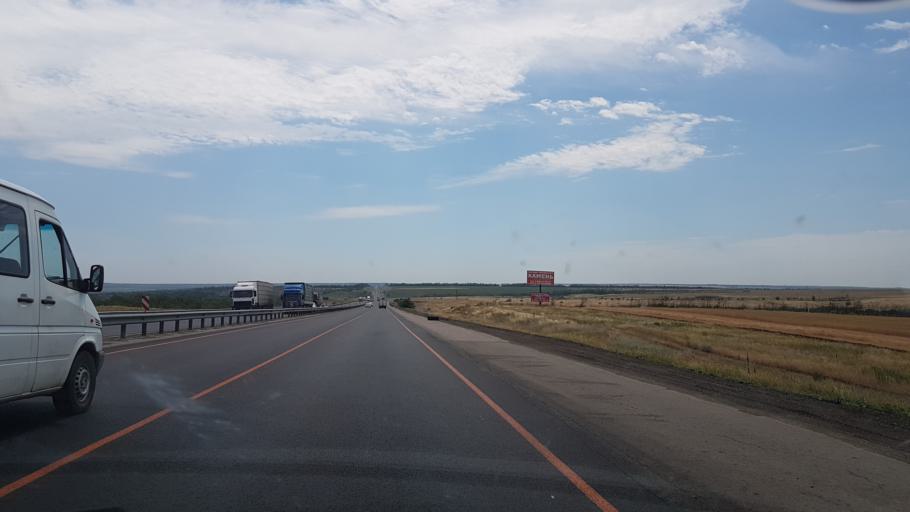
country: RU
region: Rostov
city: Gornyy
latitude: 47.9358
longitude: 40.2180
